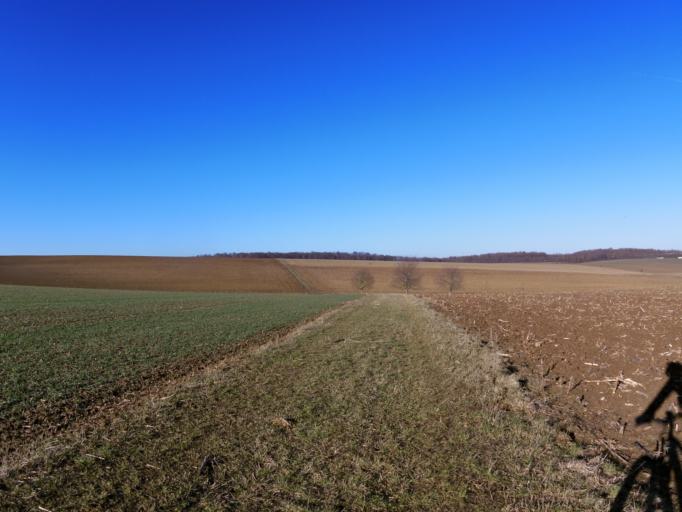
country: DE
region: Bavaria
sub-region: Regierungsbezirk Unterfranken
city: Estenfeld
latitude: 49.8441
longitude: 9.9947
